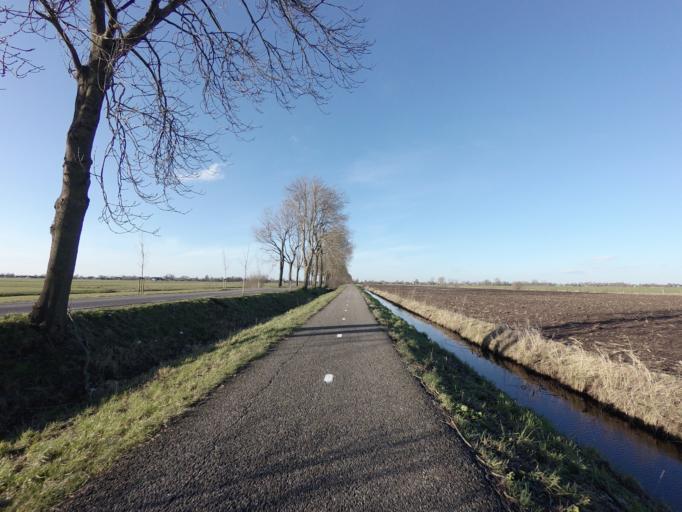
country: NL
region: Utrecht
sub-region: Gemeente Lopik
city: Lopik
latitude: 51.9877
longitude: 4.9089
